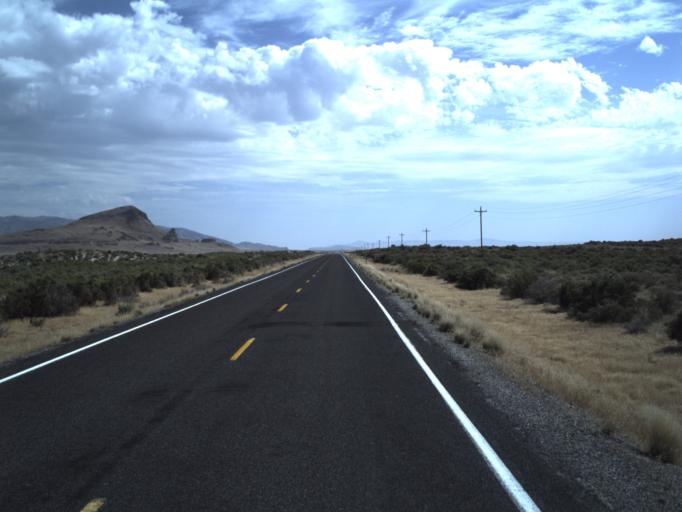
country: US
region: Utah
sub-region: Tooele County
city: Wendover
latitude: 41.4225
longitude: -113.8799
